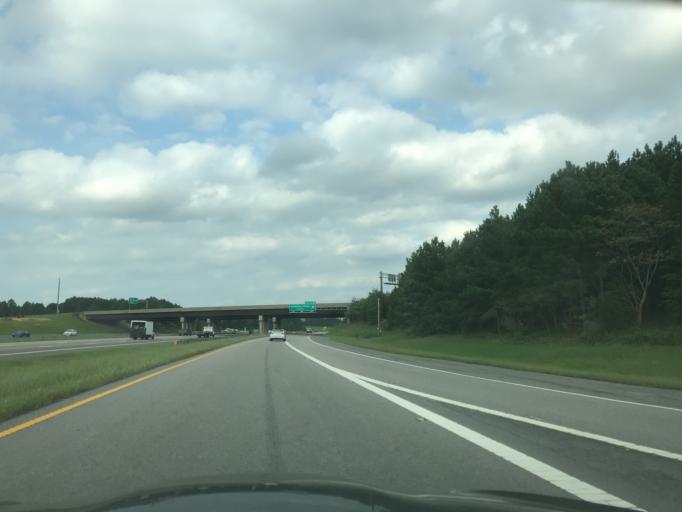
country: US
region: North Carolina
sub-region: Wake County
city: Morrisville
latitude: 35.8903
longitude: -78.8154
